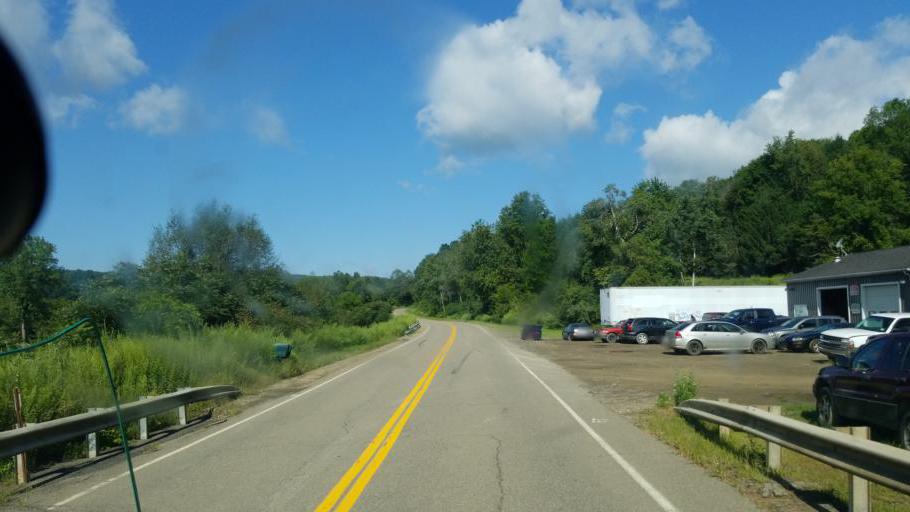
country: US
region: New York
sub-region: Steuben County
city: Canisteo
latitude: 42.2659
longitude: -77.5814
